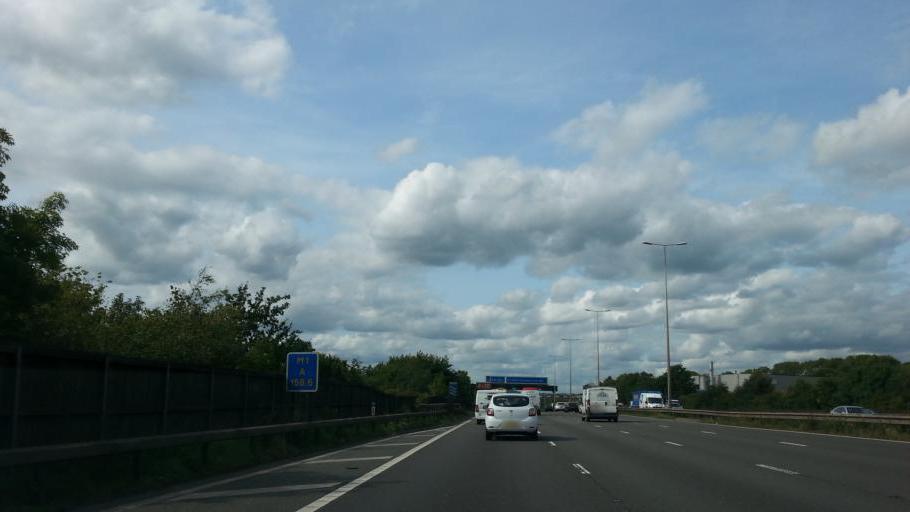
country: GB
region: England
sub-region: Leicestershire
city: Kirby Muxloe
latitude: 52.6293
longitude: -1.2133
